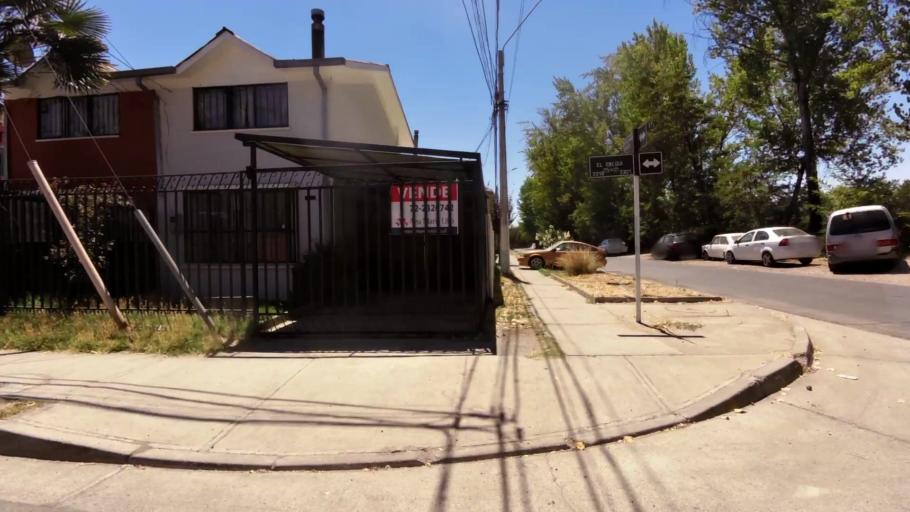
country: CL
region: O'Higgins
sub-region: Provincia de Cachapoal
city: Rancagua
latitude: -34.1592
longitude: -70.7595
